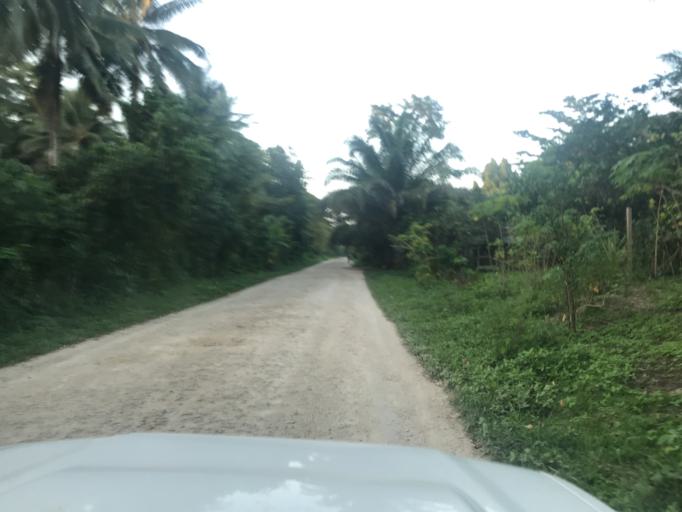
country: VU
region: Sanma
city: Luganville
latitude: -15.5676
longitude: 166.9578
